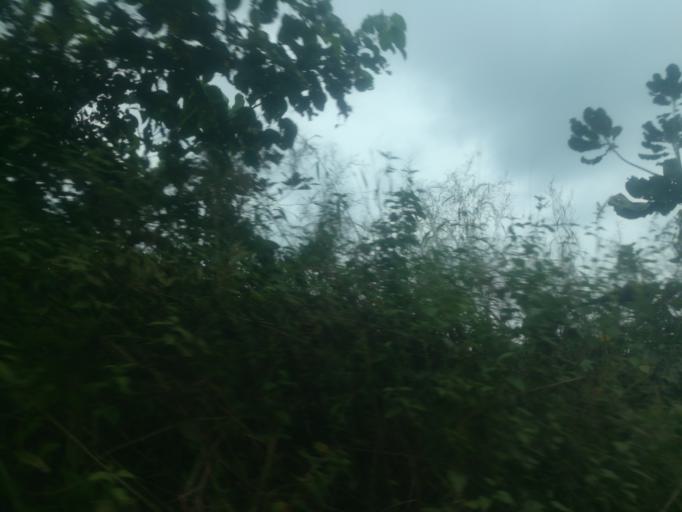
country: NG
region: Ogun
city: Ayetoro
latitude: 7.1033
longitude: 3.1486
